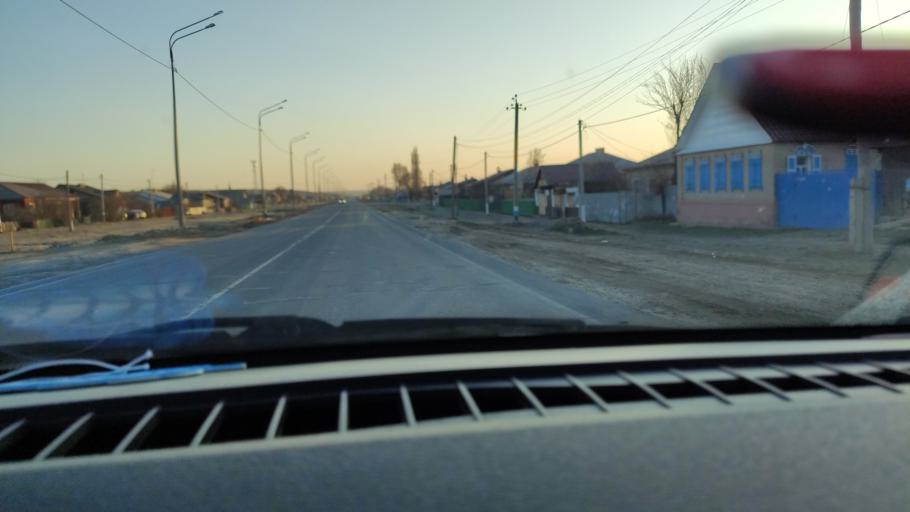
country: RU
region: Saratov
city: Sinodskoye
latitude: 51.9913
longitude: 46.6689
